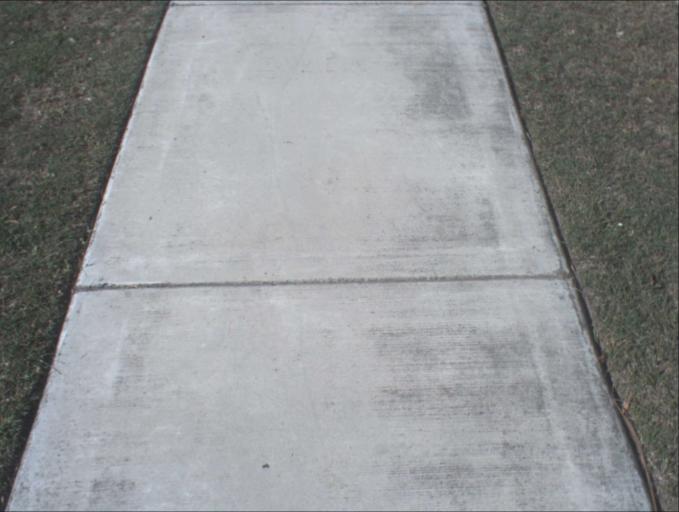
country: AU
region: Queensland
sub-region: Logan
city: Park Ridge South
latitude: -27.6776
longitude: 153.0581
